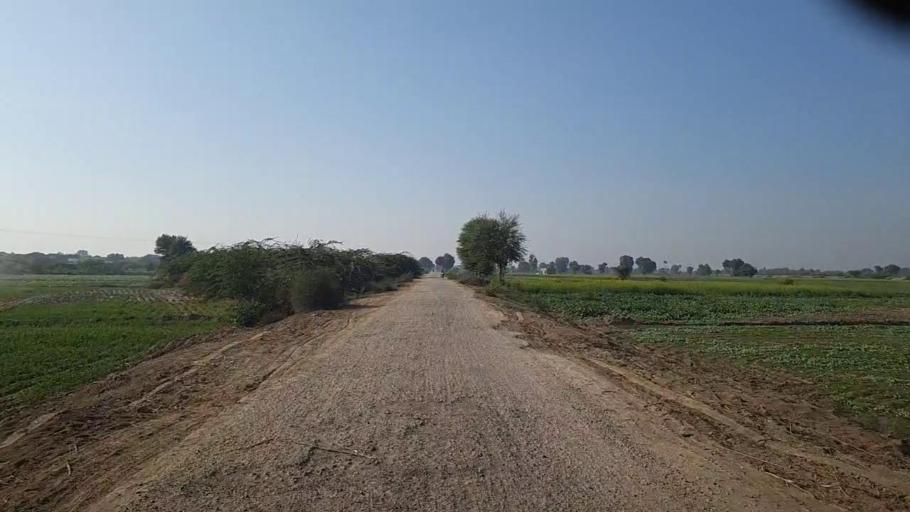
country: PK
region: Sindh
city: Darya Khan Marri
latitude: 26.6833
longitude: 68.3603
